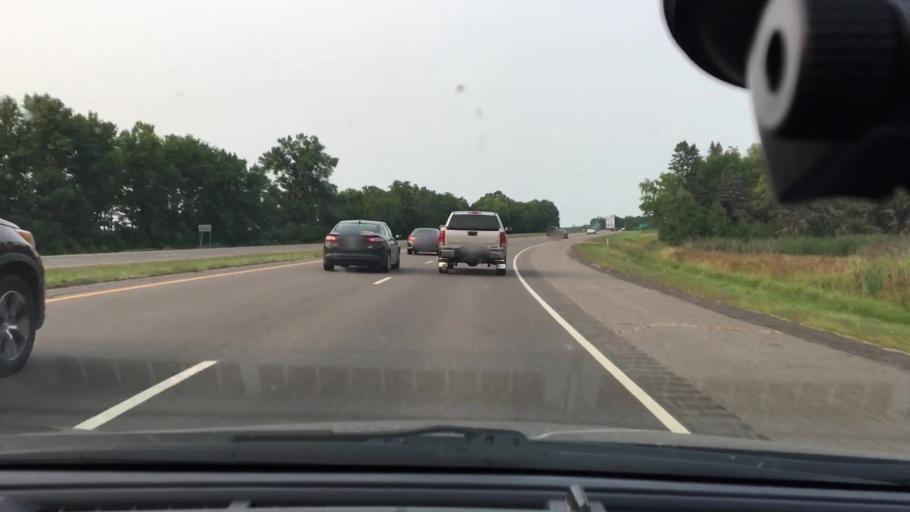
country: US
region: Minnesota
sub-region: Mille Lacs County
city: Vineland
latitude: 46.0748
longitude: -93.6564
